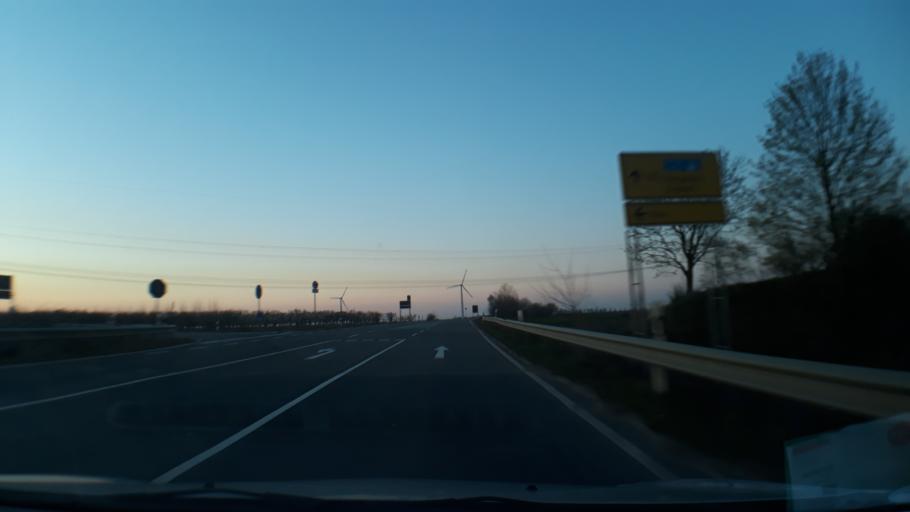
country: DE
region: North Rhine-Westphalia
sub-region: Regierungsbezirk Koln
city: Norvenich
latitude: 50.8537
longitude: 6.6133
